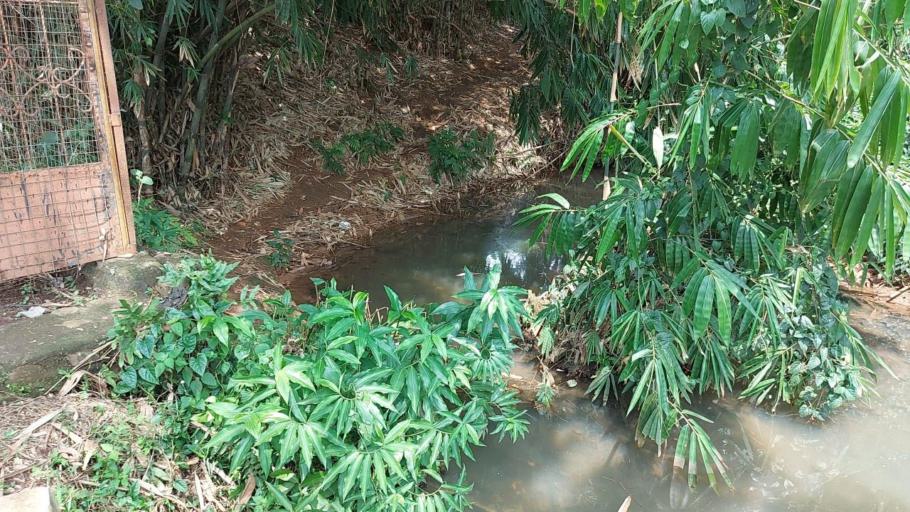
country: ID
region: West Java
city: Cibinong
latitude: -6.4687
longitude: 106.8095
